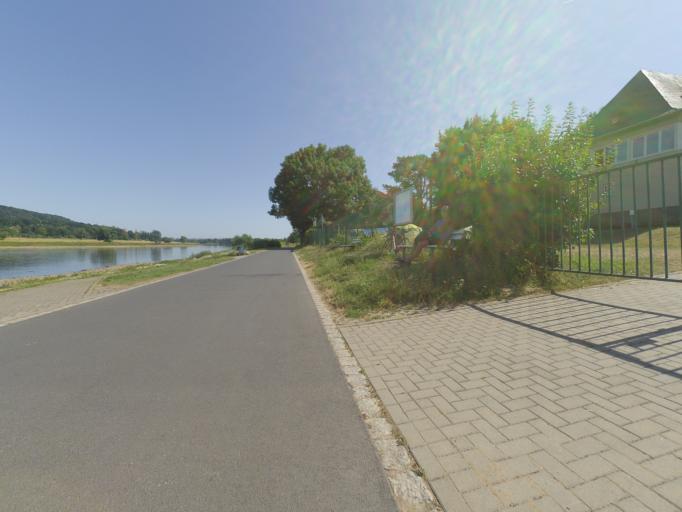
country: DE
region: Saxony
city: Albertstadt
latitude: 51.0462
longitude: 13.8147
